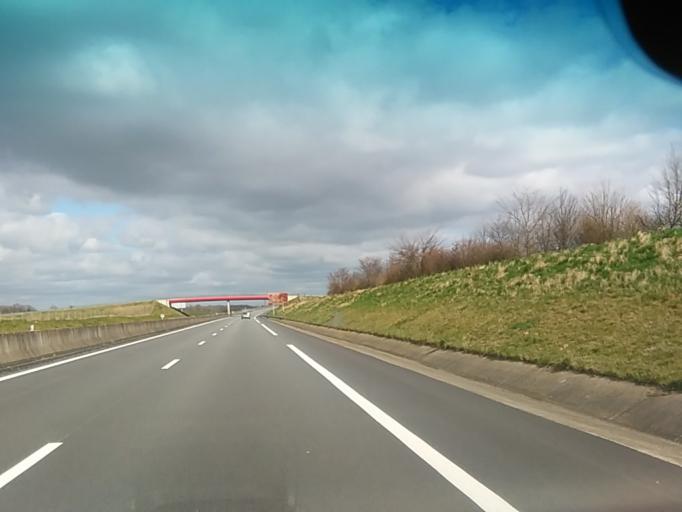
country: FR
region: Haute-Normandie
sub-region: Departement de l'Eure
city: Thiberville
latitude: 49.0701
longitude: 0.4714
